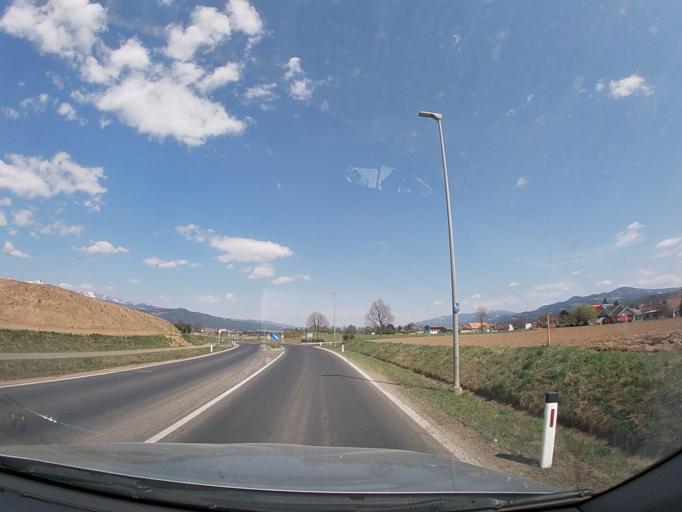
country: AT
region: Styria
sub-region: Politischer Bezirk Murtal
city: Zeltweg
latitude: 47.1690
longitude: 14.7457
